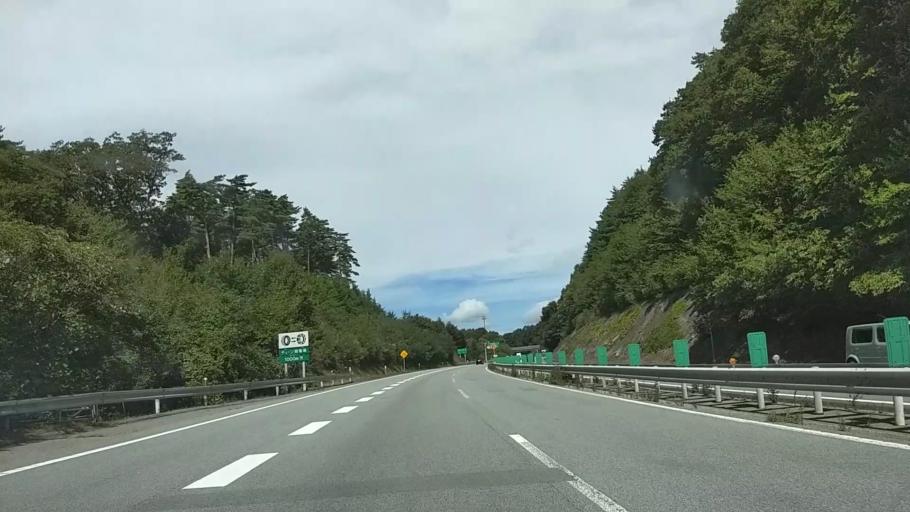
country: JP
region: Yamanashi
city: Nirasaki
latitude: 35.8623
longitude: 138.3279
